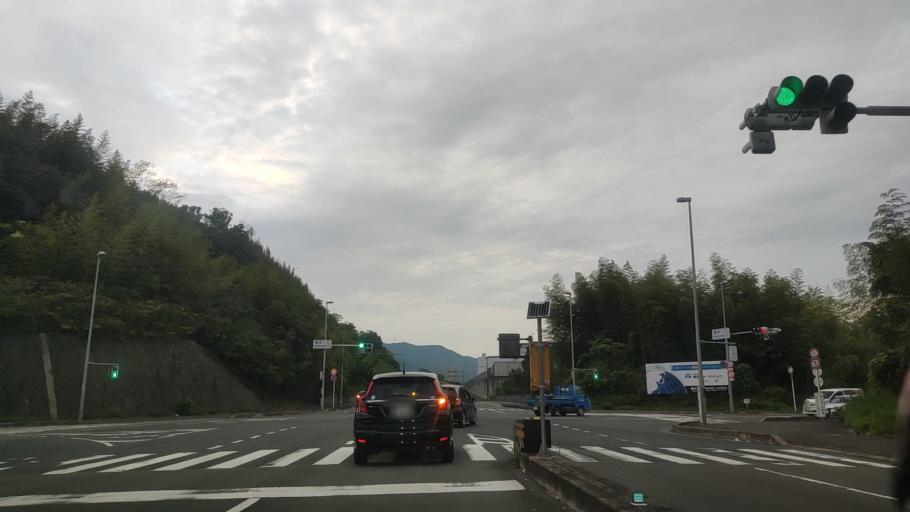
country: JP
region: Wakayama
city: Hashimoto
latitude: 34.3233
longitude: 135.6058
